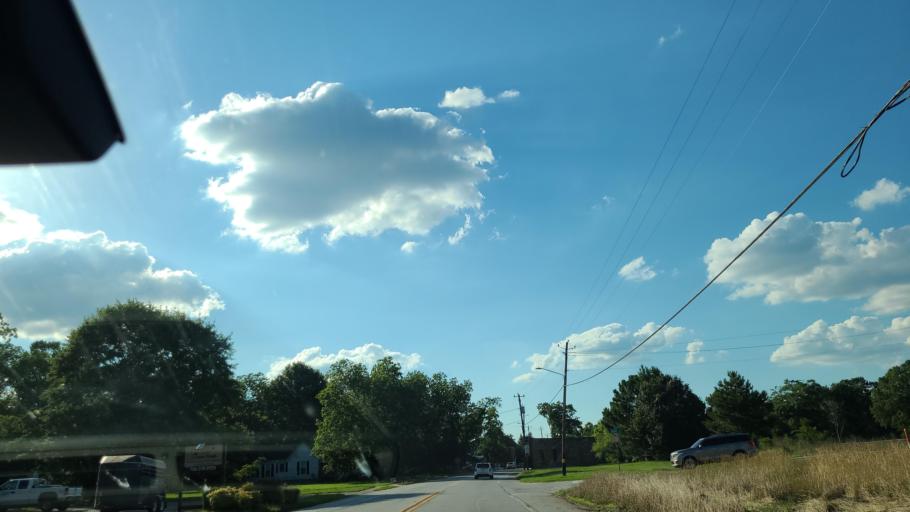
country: US
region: Georgia
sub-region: Oconee County
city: Watkinsville
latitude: 33.8150
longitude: -83.4357
